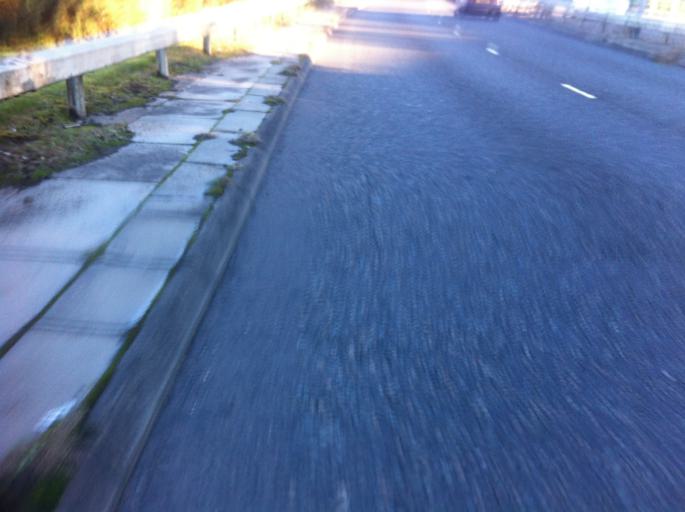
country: GB
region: Scotland
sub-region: Glasgow City
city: Glasgow
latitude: 55.8812
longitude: -4.2342
